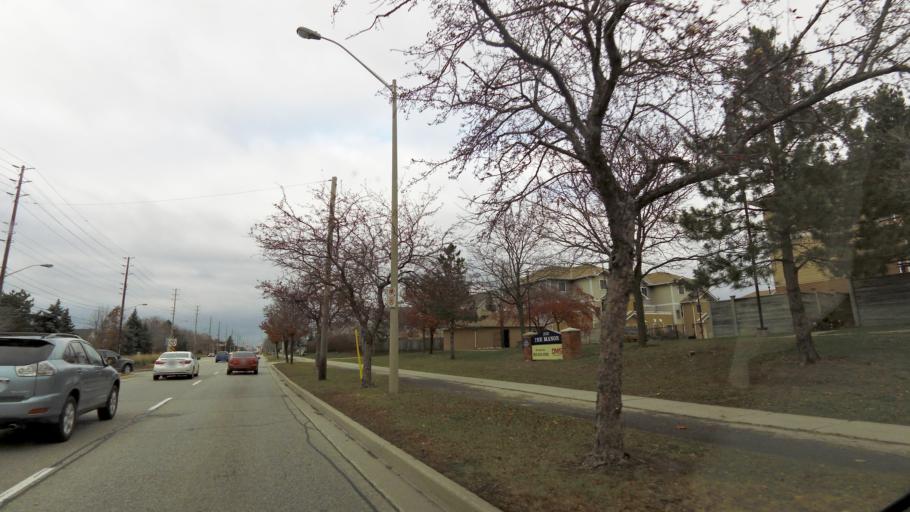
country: CA
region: Ontario
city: Burlington
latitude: 43.3799
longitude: -79.8072
